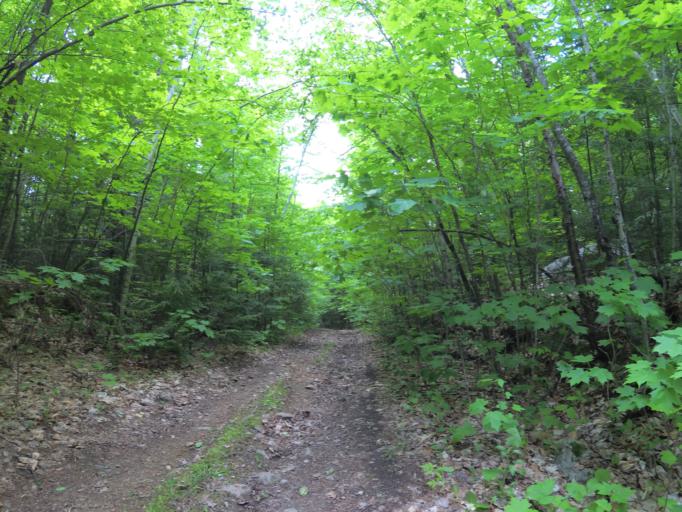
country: CA
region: Ontario
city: Renfrew
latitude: 45.0569
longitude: -76.8693
